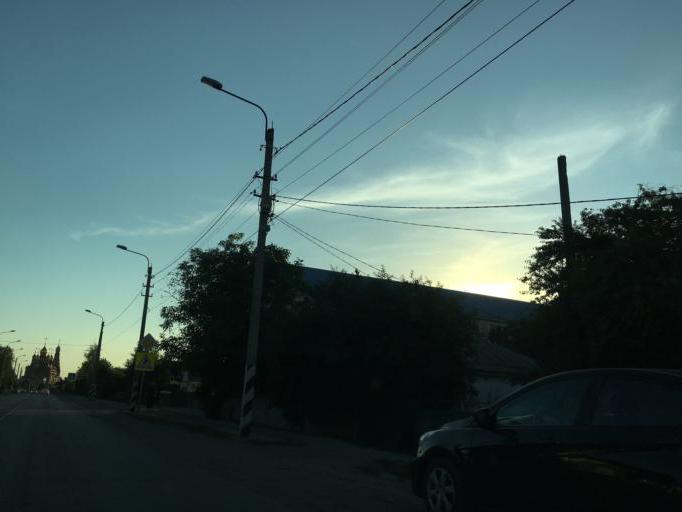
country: RU
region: Krasnodarskiy
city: Kushchevskaya
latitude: 46.5689
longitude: 39.6480
